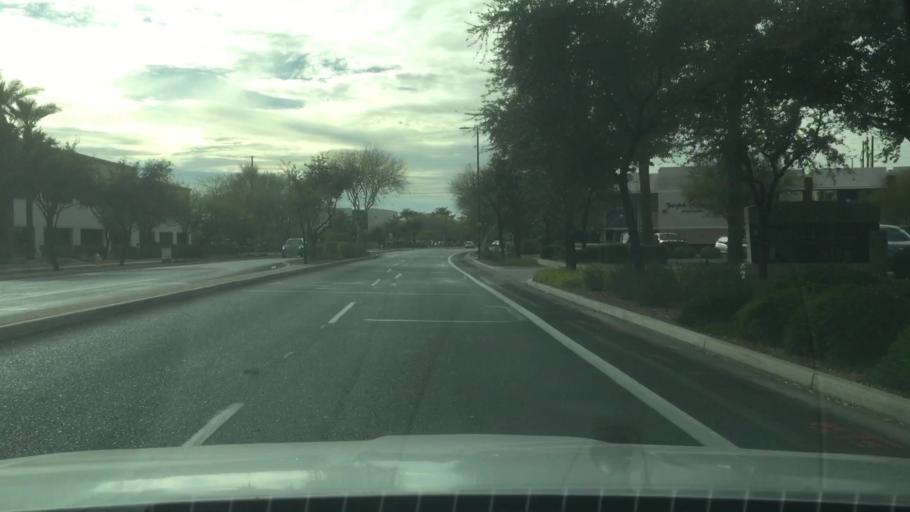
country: US
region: Arizona
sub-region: Maricopa County
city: Guadalupe
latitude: 33.4033
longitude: -111.9808
